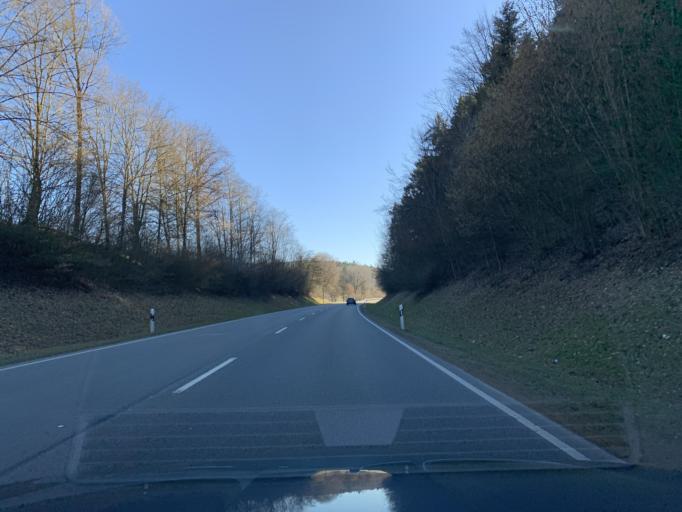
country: DE
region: Bavaria
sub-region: Upper Palatinate
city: Schonthal
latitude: 49.3256
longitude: 12.6328
